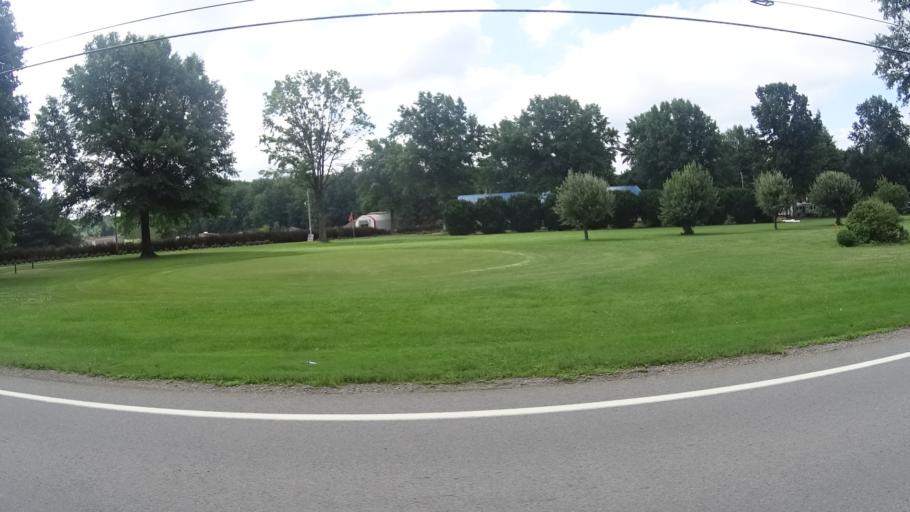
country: US
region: Ohio
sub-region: Huron County
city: Wakeman
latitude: 41.3172
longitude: -82.4311
